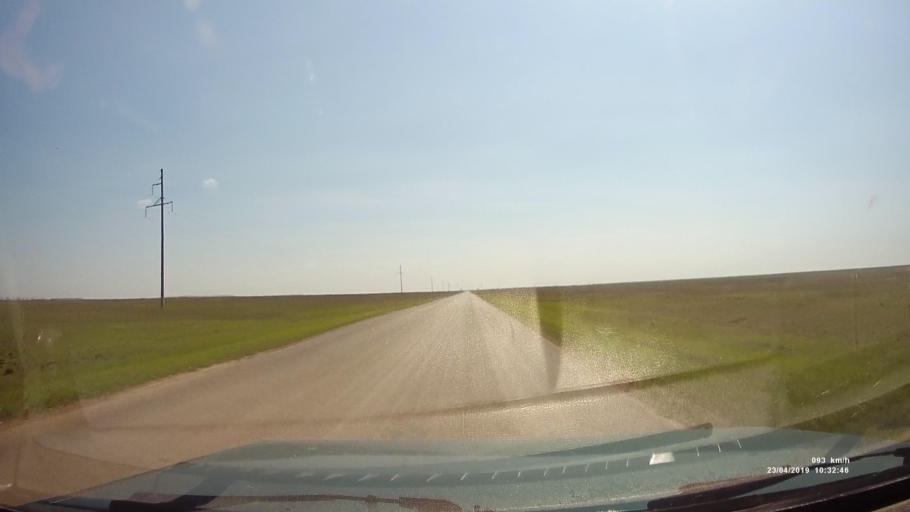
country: RU
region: Kalmykiya
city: Yashalta
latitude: 46.5781
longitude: 42.5840
